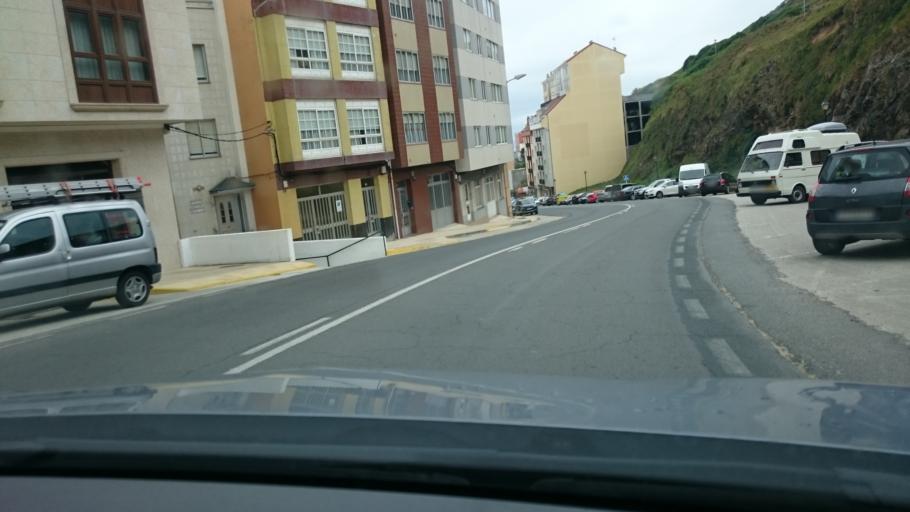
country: ES
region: Galicia
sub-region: Provincia da Coruna
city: Malpica
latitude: 43.3224
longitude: -8.8165
